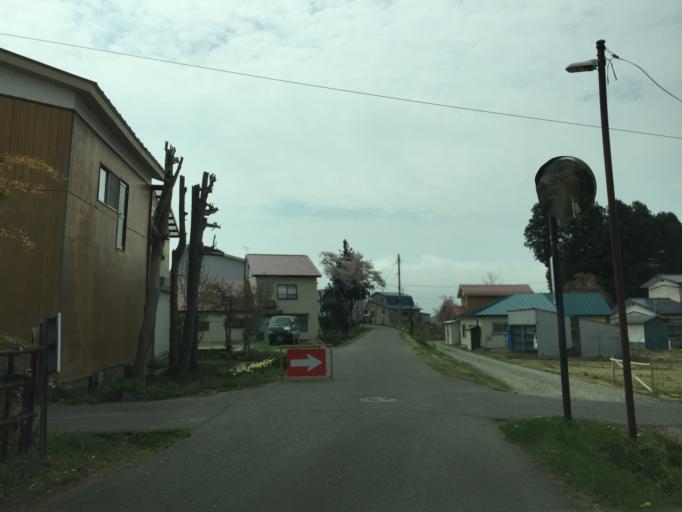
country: JP
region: Fukushima
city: Inawashiro
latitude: 37.5389
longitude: 140.1383
